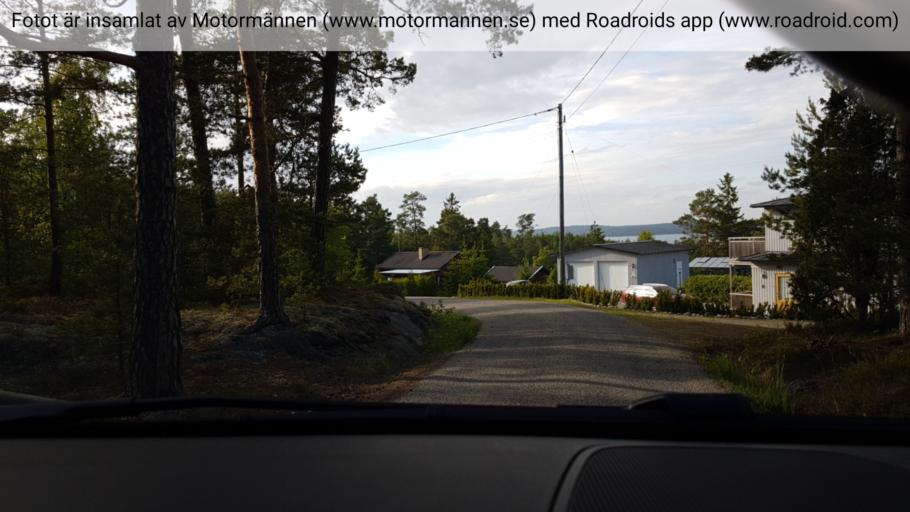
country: SE
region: Stockholm
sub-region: Haninge Kommun
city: Jordbro
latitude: 59.0180
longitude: 18.1040
